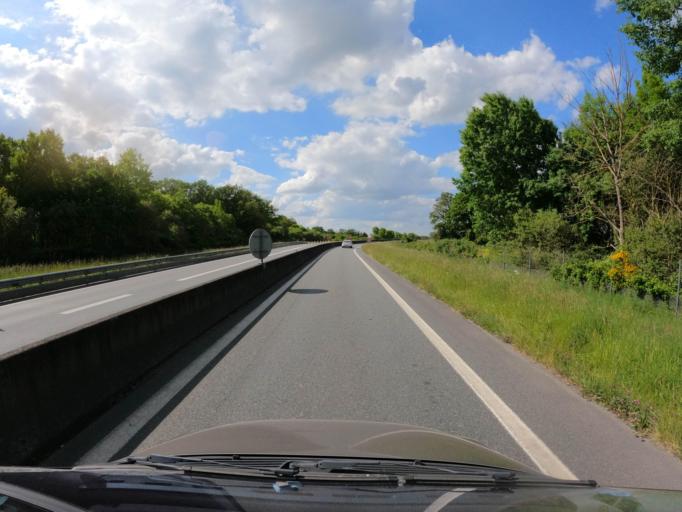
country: FR
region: Pays de la Loire
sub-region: Departement de Maine-et-Loire
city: La Tessoualle
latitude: 47.0221
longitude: -0.8838
